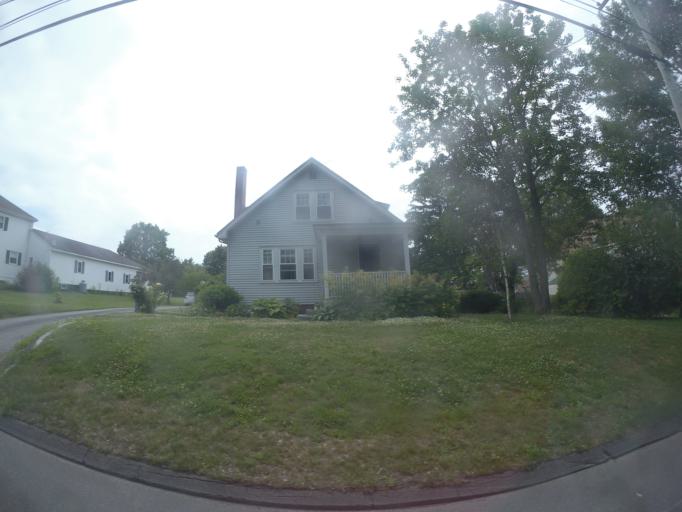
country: US
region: Maine
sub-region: Cumberland County
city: Falmouth
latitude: 43.7202
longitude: -70.2296
